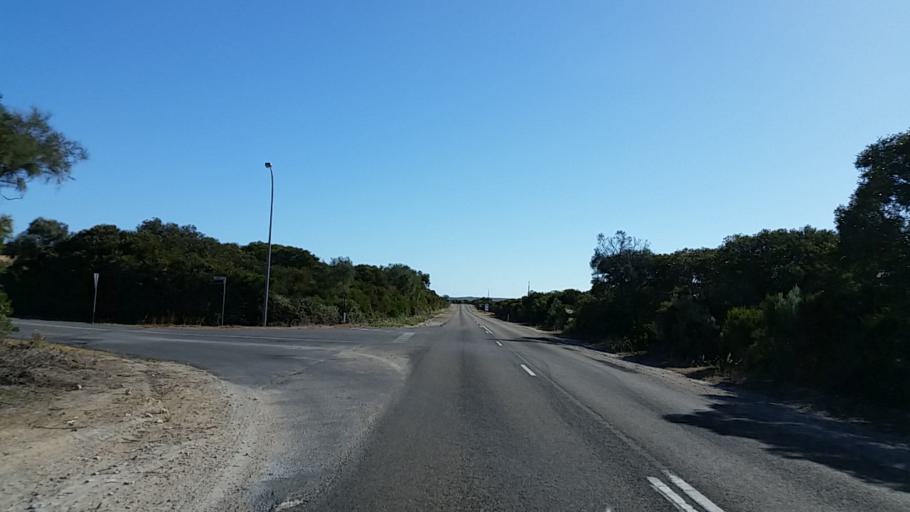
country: AU
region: South Australia
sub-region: Yorke Peninsula
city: Honiton
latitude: -35.2490
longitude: 136.9685
